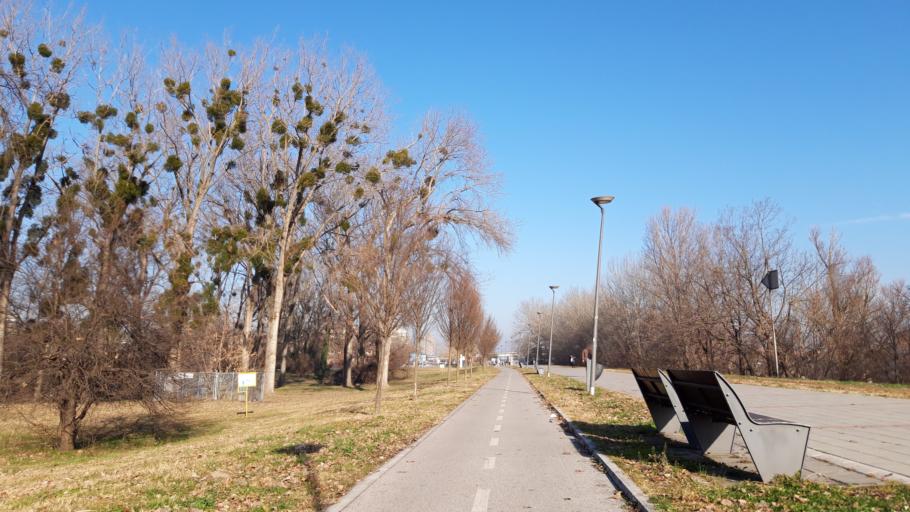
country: RS
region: Autonomna Pokrajina Vojvodina
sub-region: Juznobacki Okrug
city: Novi Sad
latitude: 45.2480
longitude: 19.8556
